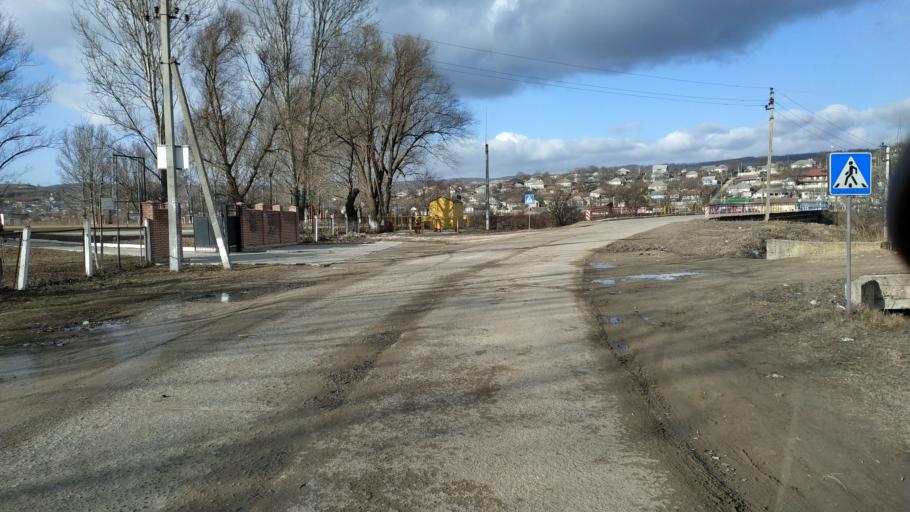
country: MD
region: Calarasi
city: Calarasi
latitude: 47.2823
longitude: 28.1977
